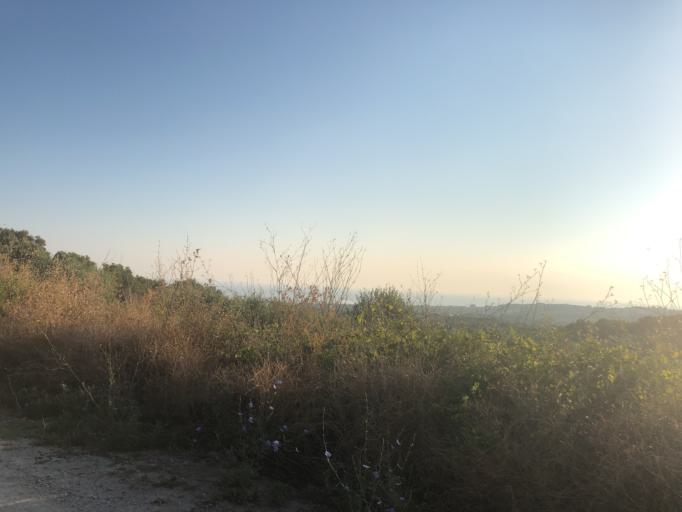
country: GR
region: Crete
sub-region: Nomos Chanias
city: Georgioupolis
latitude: 35.3330
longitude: 24.2924
